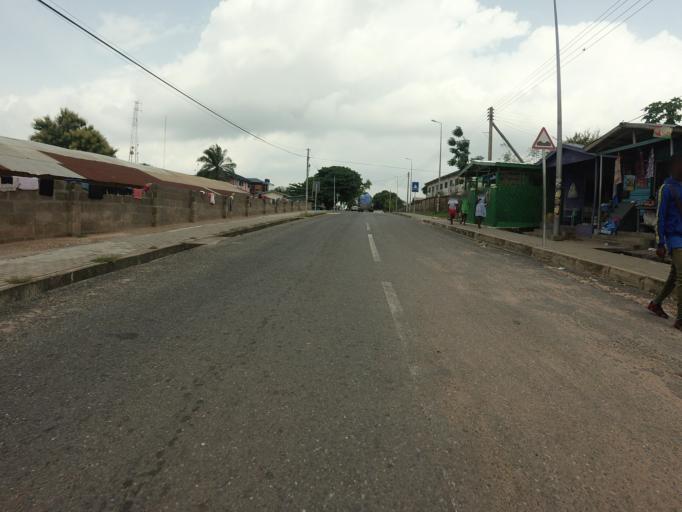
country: GH
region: Volta
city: Ho
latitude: 6.6119
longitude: 0.4682
